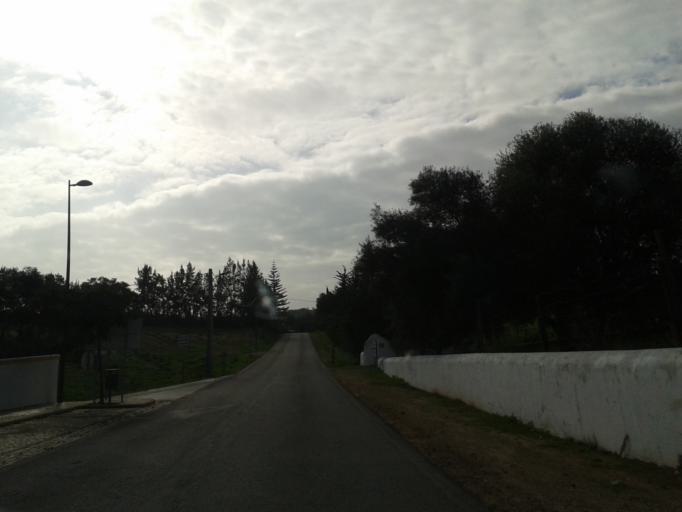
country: PT
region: Faro
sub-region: Vila Real de Santo Antonio
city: Monte Gordo
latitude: 37.1931
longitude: -7.4846
